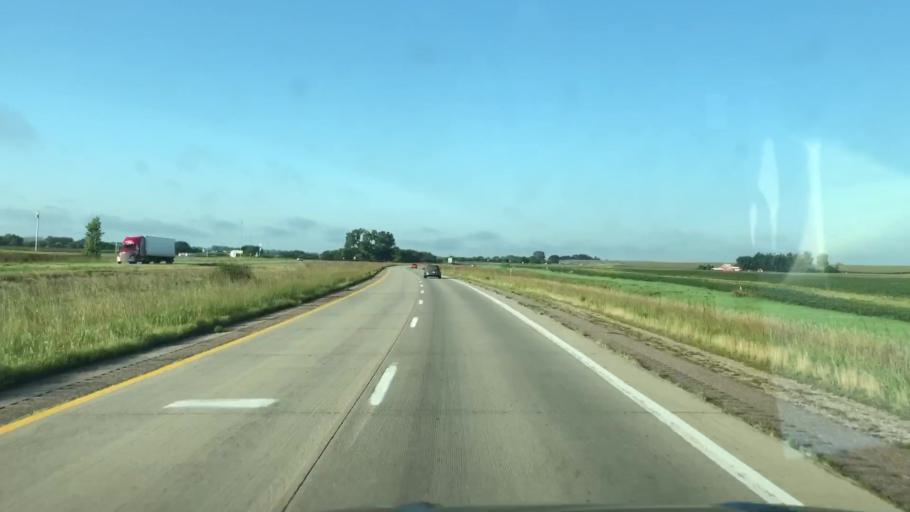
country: US
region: Iowa
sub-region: Sioux County
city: Alton
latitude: 42.9285
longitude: -96.0583
